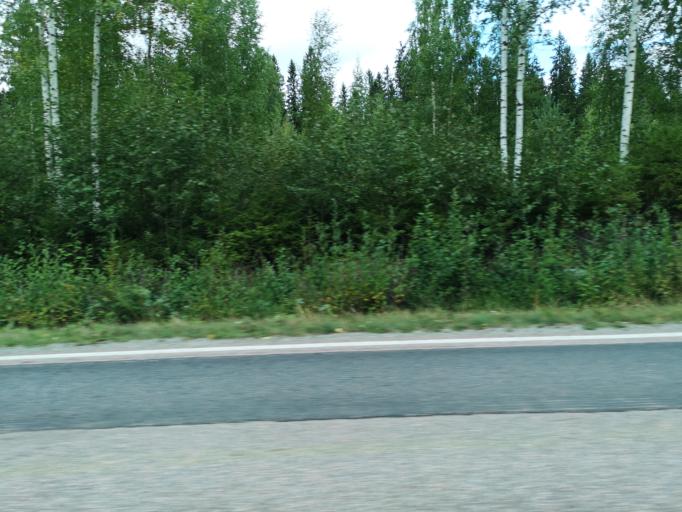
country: FI
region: Central Finland
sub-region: Jyvaeskylae
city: Hankasalmi
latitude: 62.3574
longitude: 26.4905
